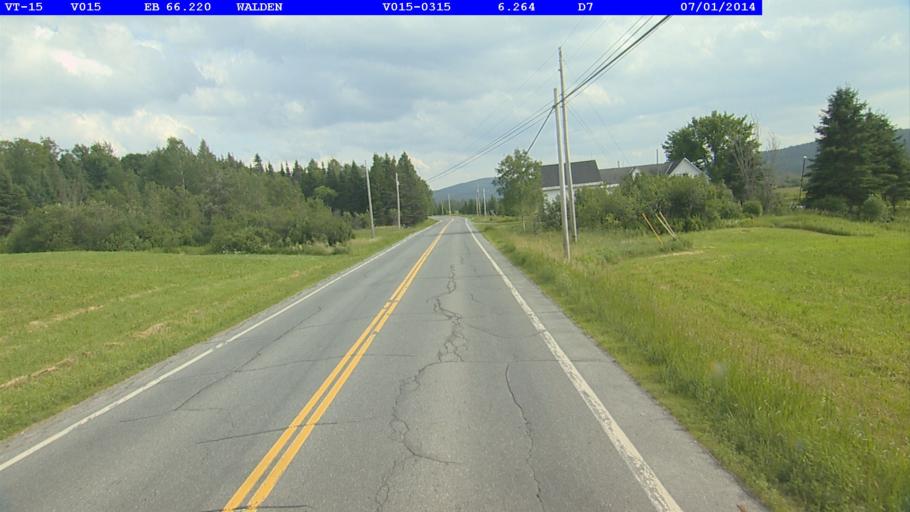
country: US
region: Vermont
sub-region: Caledonia County
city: Hardwick
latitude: 44.4352
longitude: -72.2224
